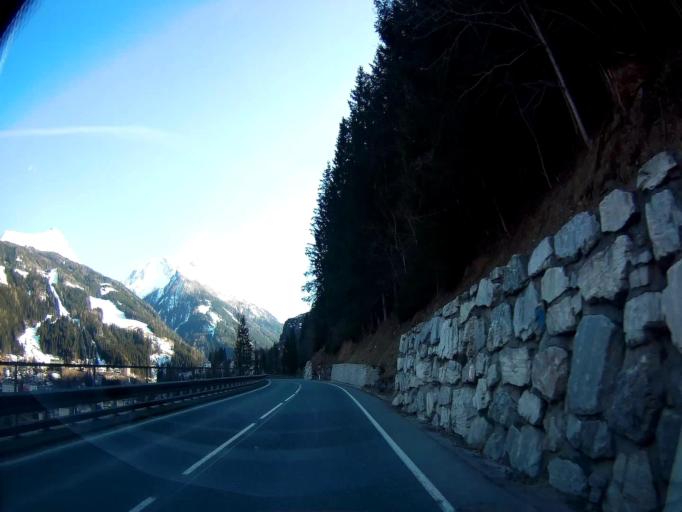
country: AT
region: Salzburg
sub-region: Politischer Bezirk Sankt Johann im Pongau
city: Bad Gastein
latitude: 47.1258
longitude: 13.1310
